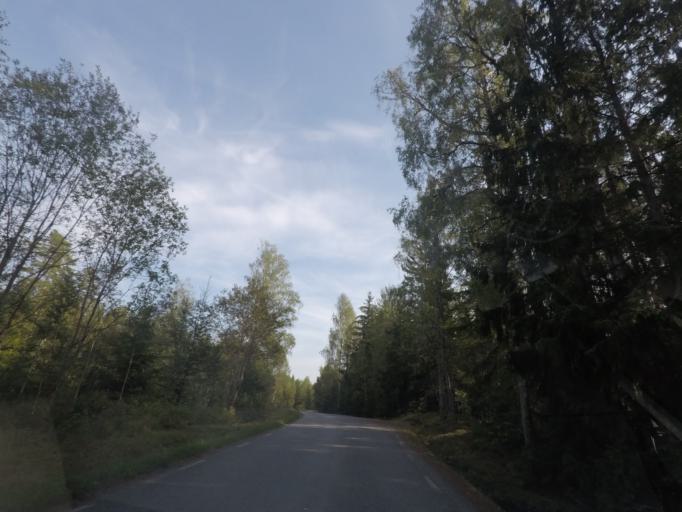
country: SE
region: Vaestmanland
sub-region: Kungsors Kommun
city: Kungsoer
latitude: 59.5109
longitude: 16.1510
